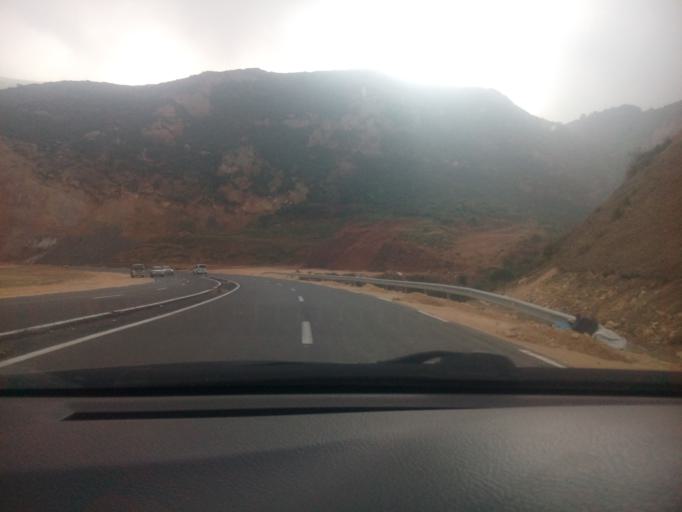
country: DZ
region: Oran
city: Mers el Kebir
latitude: 35.7178
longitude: -0.7309
